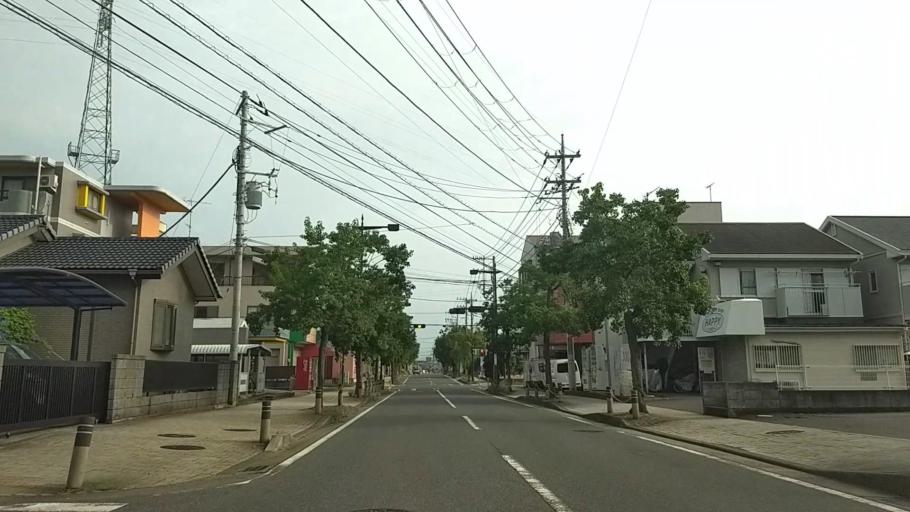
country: JP
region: Kanagawa
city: Oiso
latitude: 35.3336
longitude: 139.3101
